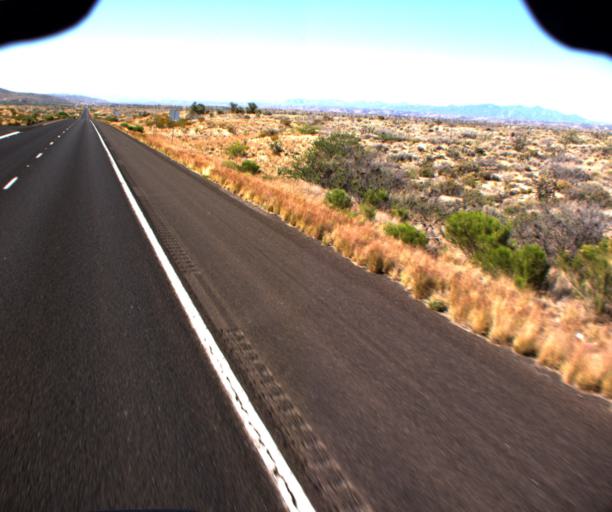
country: US
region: Arizona
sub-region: Mohave County
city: Kingman
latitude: 35.0685
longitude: -113.6658
